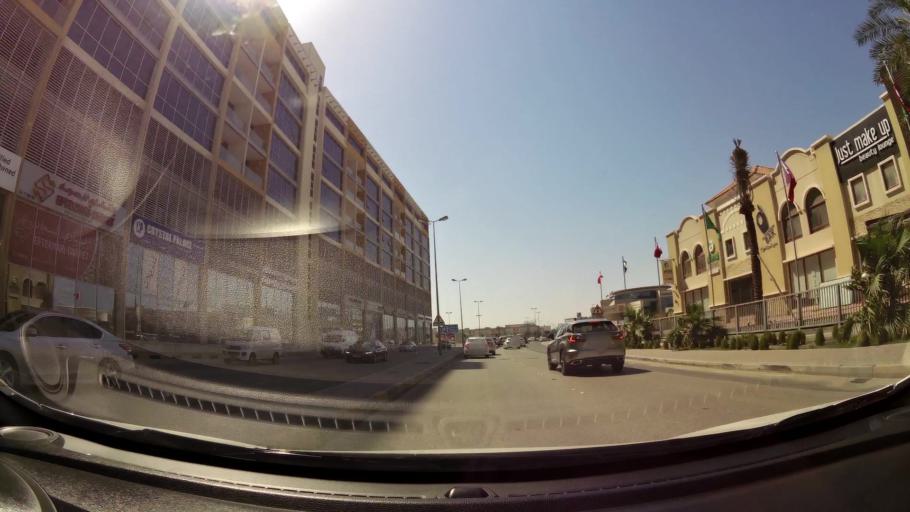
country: BH
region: Manama
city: Manama
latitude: 26.2126
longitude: 50.5771
